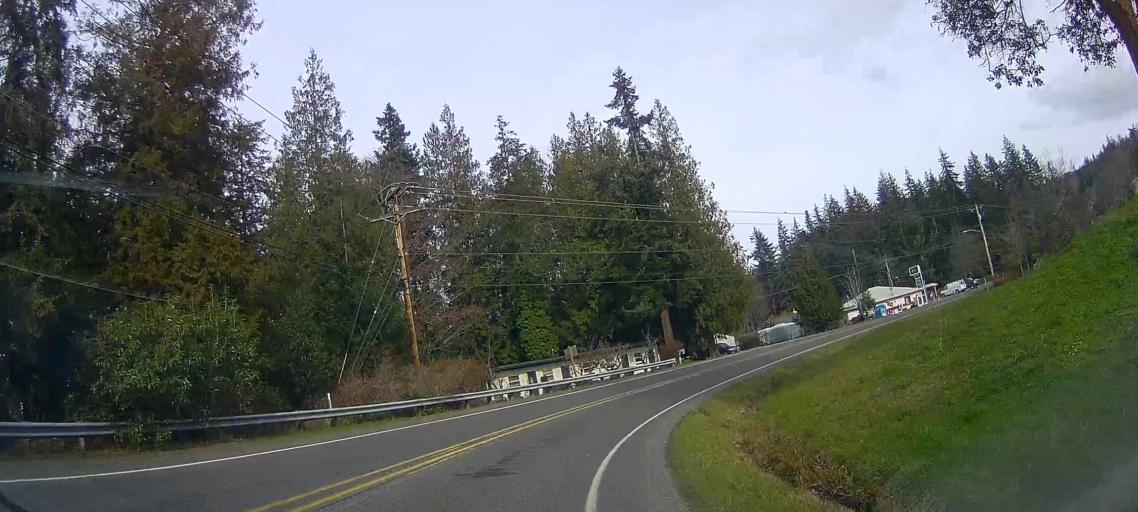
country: US
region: Washington
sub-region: Island County
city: Camano
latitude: 48.2474
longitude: -122.5204
